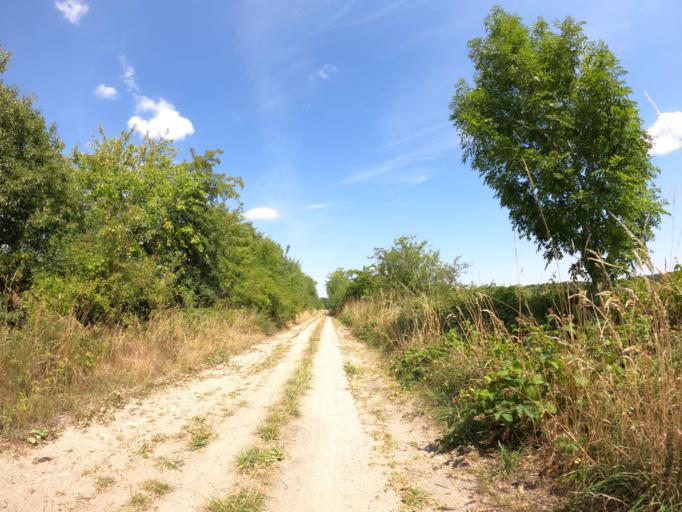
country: DE
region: Brandenburg
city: Mittenwalde
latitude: 53.2779
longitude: 13.5528
